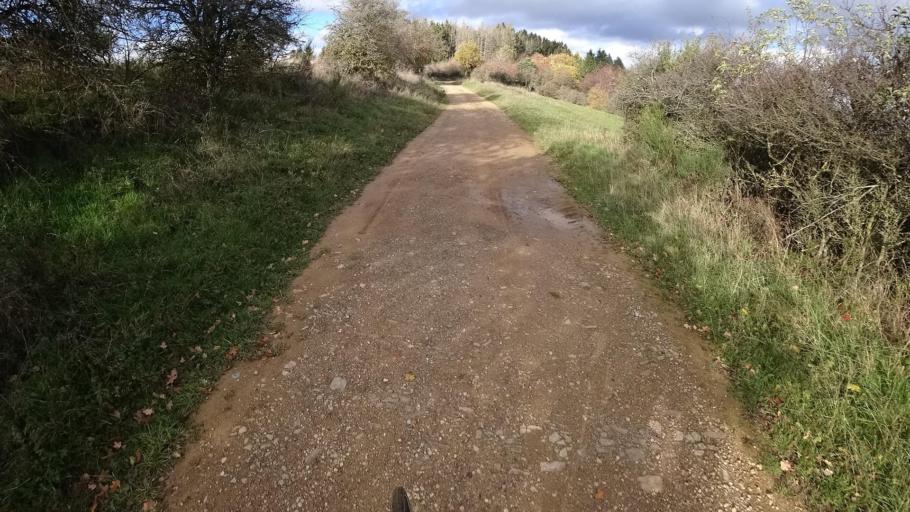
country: DE
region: Rheinland-Pfalz
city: Honningen
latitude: 50.4655
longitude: 6.9403
